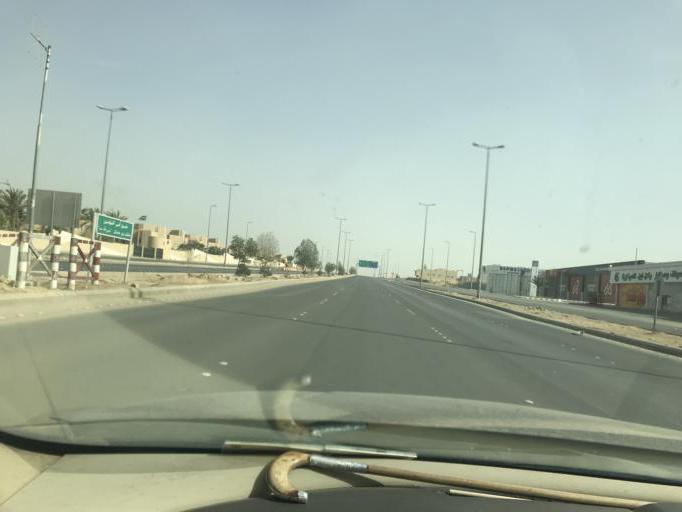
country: SA
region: Ar Riyad
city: Riyadh
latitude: 24.8270
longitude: 46.6831
